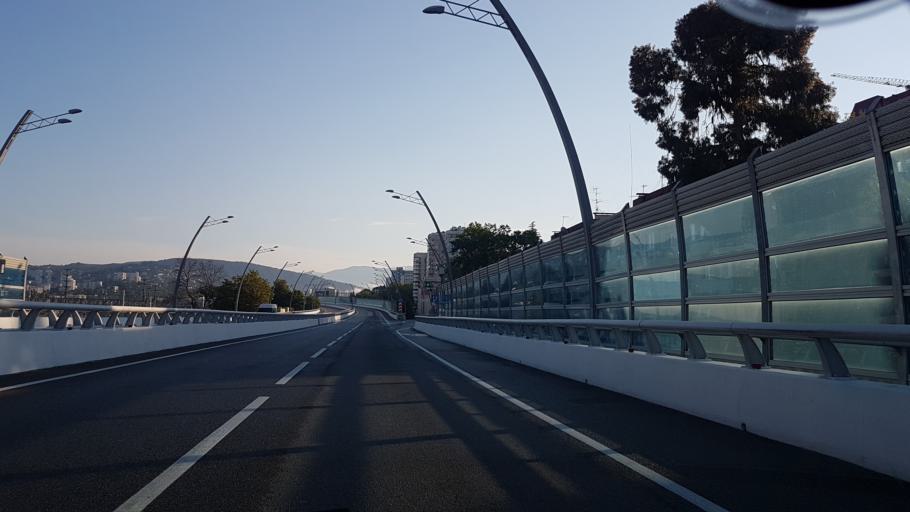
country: RU
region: Krasnodarskiy
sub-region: Sochi City
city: Sochi
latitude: 43.5924
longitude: 39.7307
